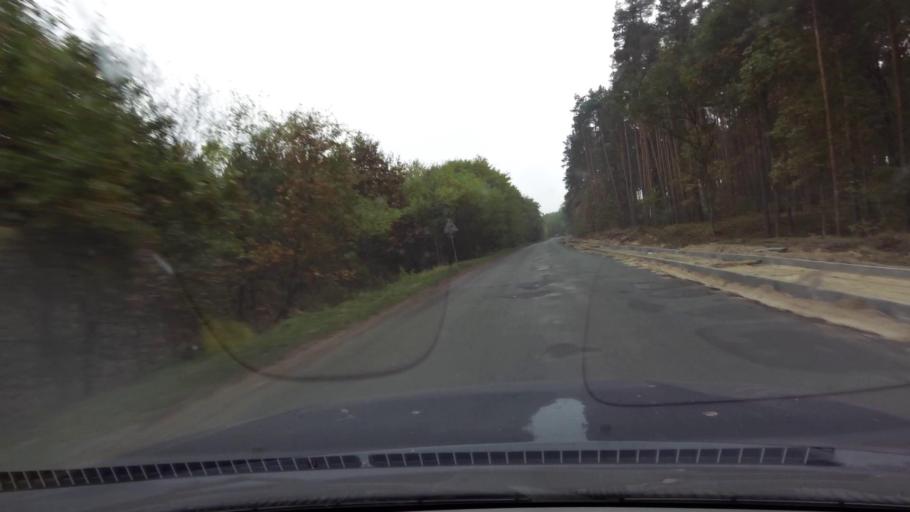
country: PL
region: West Pomeranian Voivodeship
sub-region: Powiat goleniowski
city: Goleniow
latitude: 53.5127
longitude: 14.7433
